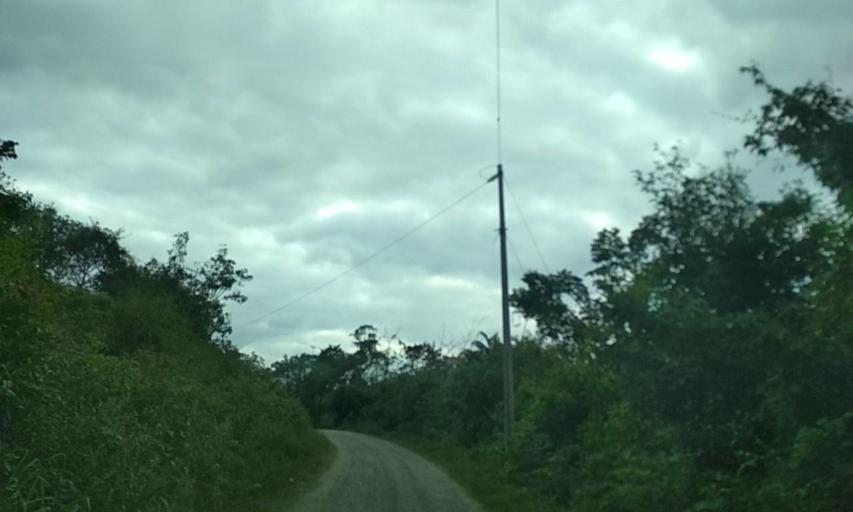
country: MX
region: Veracruz
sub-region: Papantla
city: Polutla
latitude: 20.5111
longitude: -97.2978
